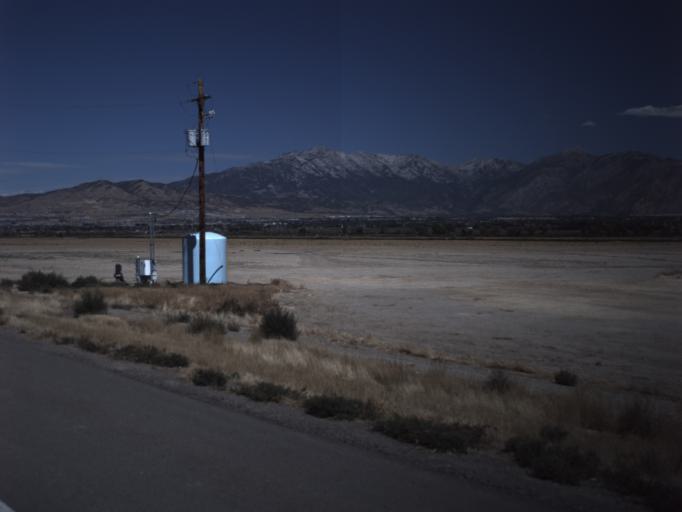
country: US
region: Utah
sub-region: Utah County
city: Saratoga Springs
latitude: 40.3600
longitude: -111.9162
